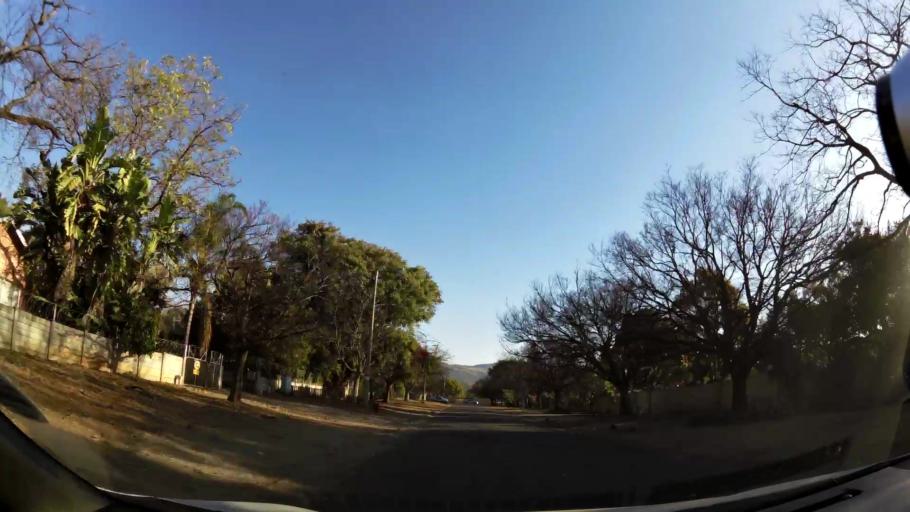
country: ZA
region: North-West
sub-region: Bojanala Platinum District Municipality
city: Rustenburg
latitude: -25.6826
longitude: 27.2243
